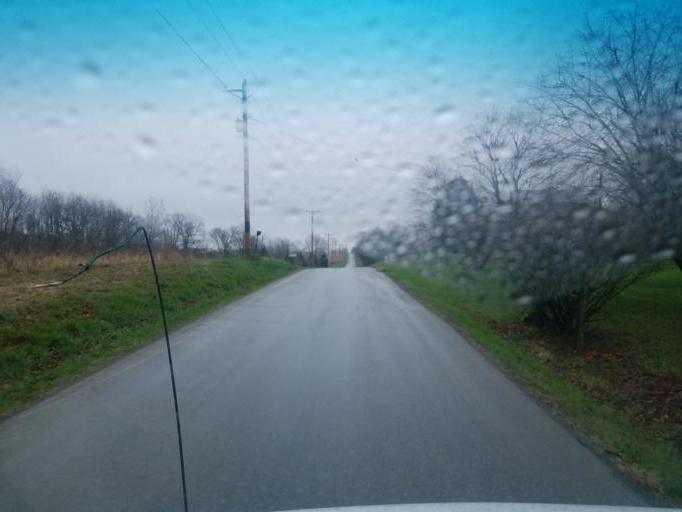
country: US
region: Ohio
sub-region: Seneca County
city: Tiffin
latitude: 40.9643
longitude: -83.1579
